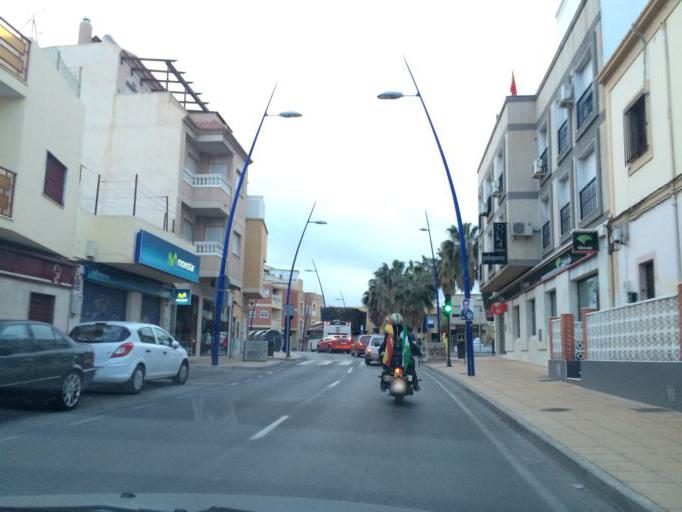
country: ES
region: Andalusia
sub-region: Provincia de Almeria
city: Almeria
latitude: 36.8406
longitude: -2.4074
